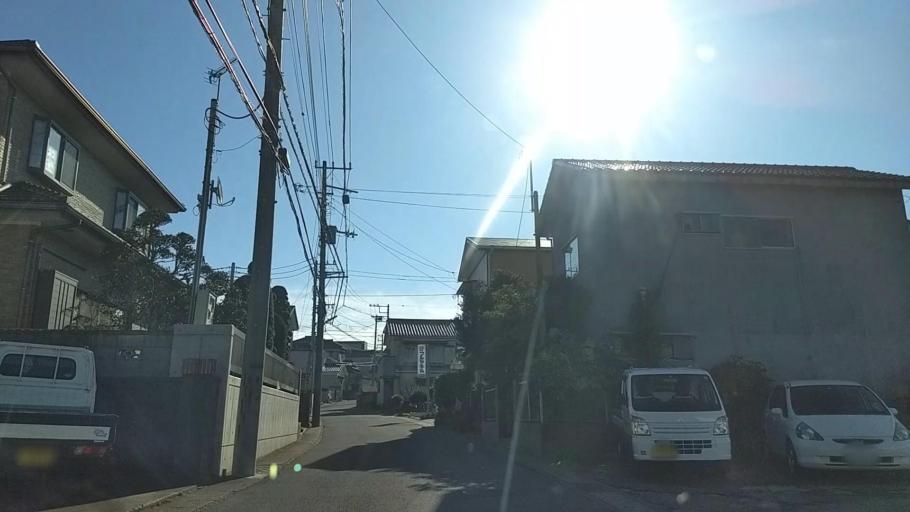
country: JP
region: Chiba
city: Hasaki
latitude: 35.7259
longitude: 140.8406
